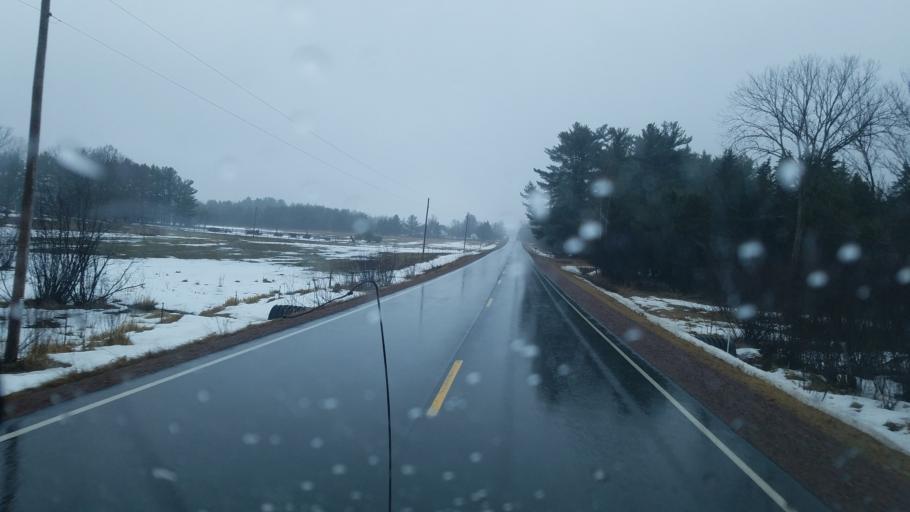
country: US
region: Wisconsin
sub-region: Wood County
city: Marshfield
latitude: 44.5668
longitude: -90.2997
